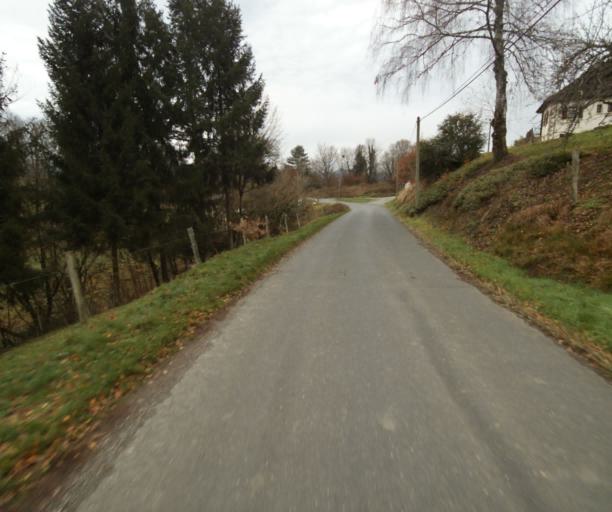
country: FR
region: Limousin
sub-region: Departement de la Correze
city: Tulle
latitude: 45.2478
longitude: 1.7357
